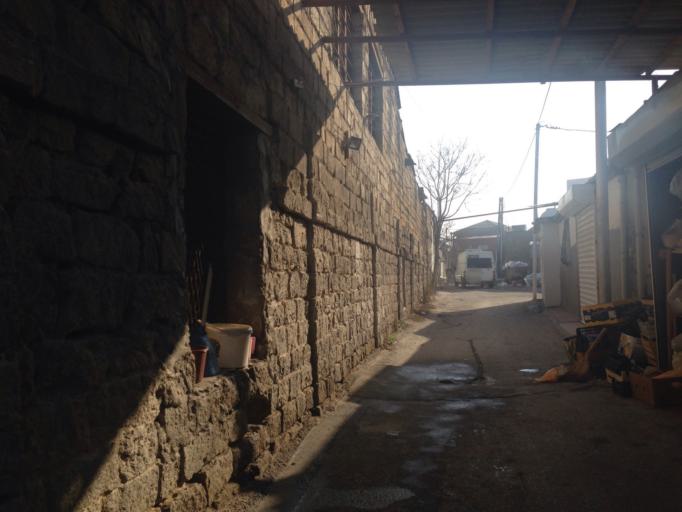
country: AZ
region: Baki
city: Baku
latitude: 40.3951
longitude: 49.8828
